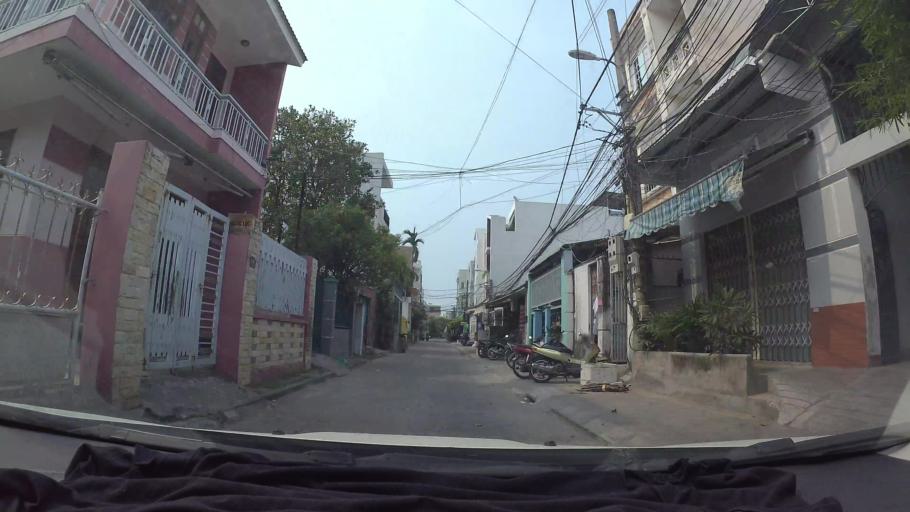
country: VN
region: Da Nang
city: Son Tra
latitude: 16.0411
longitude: 108.2158
